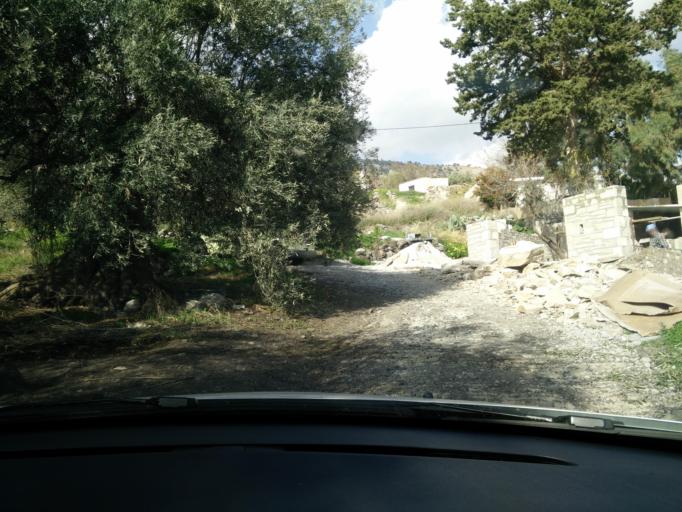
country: GR
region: Crete
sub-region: Nomos Lasithiou
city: Gra Liyia
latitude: 35.0352
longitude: 25.5740
